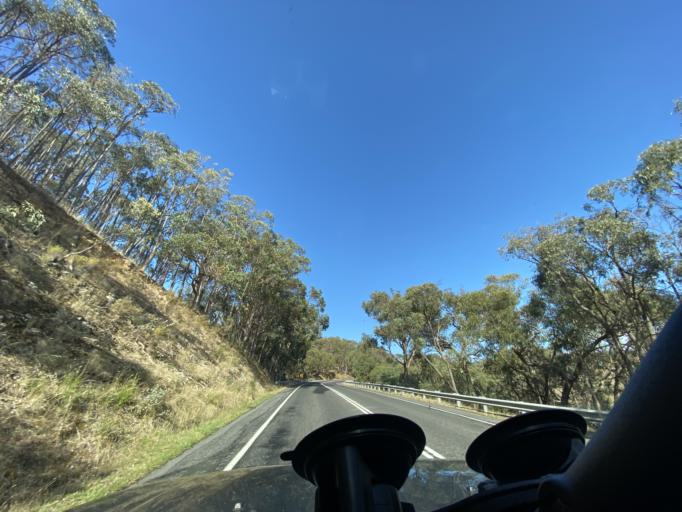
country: AU
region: Victoria
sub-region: Murrindindi
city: Kinglake West
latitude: -37.2976
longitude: 145.3779
